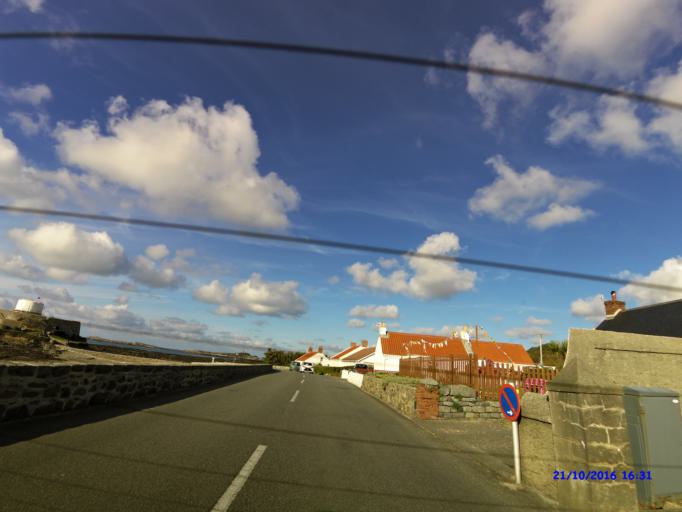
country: GG
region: St Peter Port
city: Saint Peter Port
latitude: 49.4377
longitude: -2.6534
